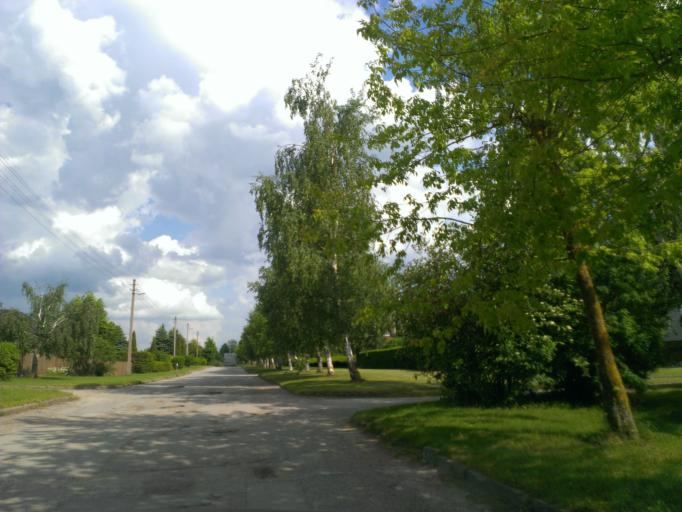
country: LT
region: Klaipedos apskritis
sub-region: Klaipeda
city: Palanga
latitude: 55.9059
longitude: 21.1311
